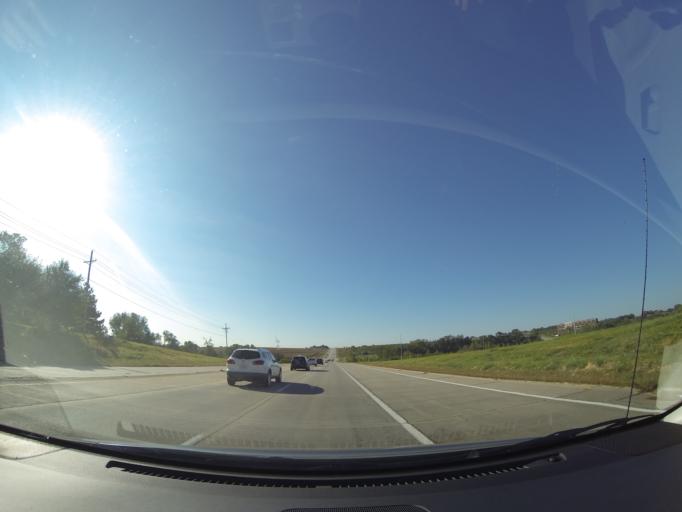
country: US
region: Nebraska
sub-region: Sarpy County
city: Gretna
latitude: 41.2022
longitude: -96.2343
